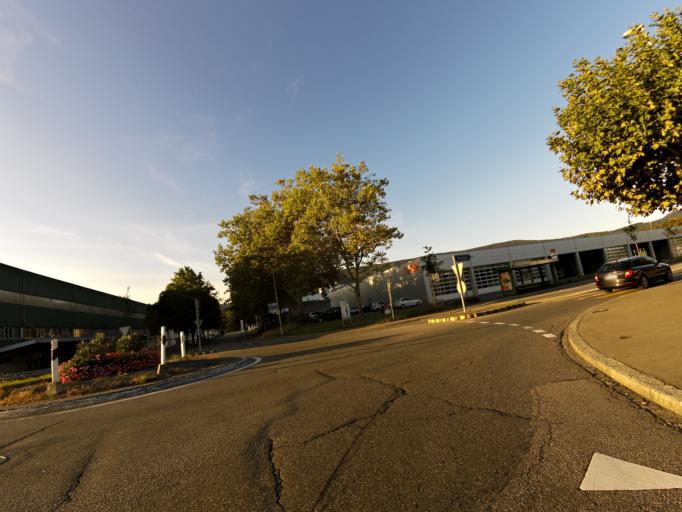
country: CH
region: Aargau
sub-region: Bezirk Aarau
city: Buchs
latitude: 47.3997
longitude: 8.0658
